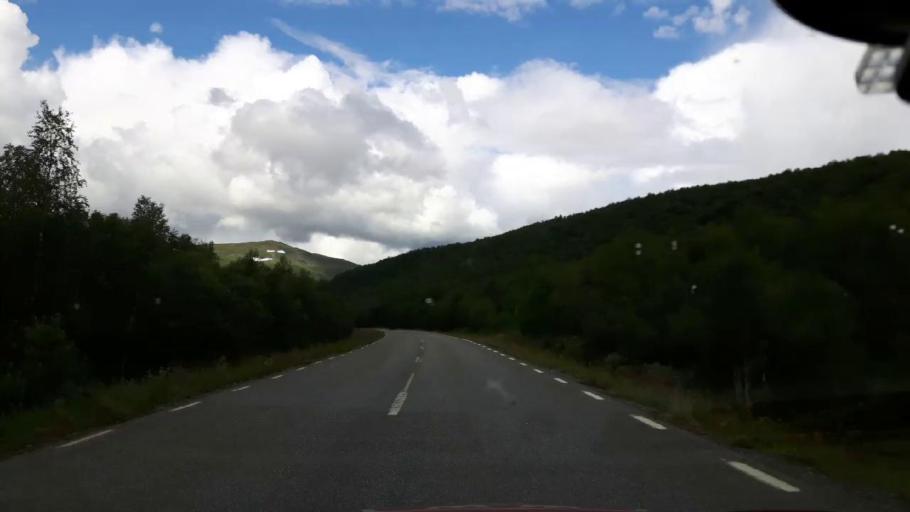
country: NO
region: Nordland
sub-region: Hattfjelldal
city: Hattfjelldal
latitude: 65.0670
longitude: 14.6848
